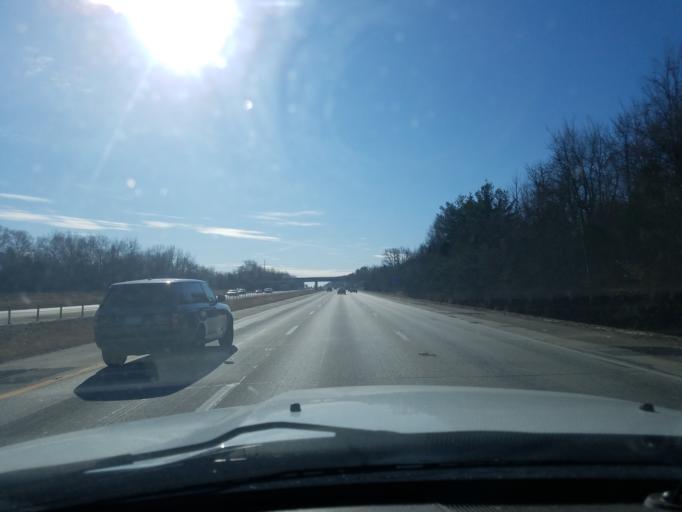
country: US
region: Kentucky
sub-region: Bullitt County
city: Hillview
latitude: 38.0942
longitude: -85.7011
